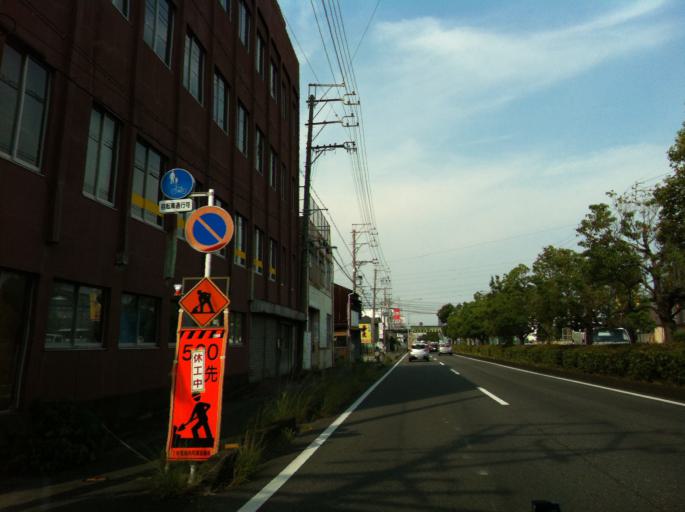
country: JP
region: Shizuoka
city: Shizuoka-shi
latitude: 34.9929
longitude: 138.4214
